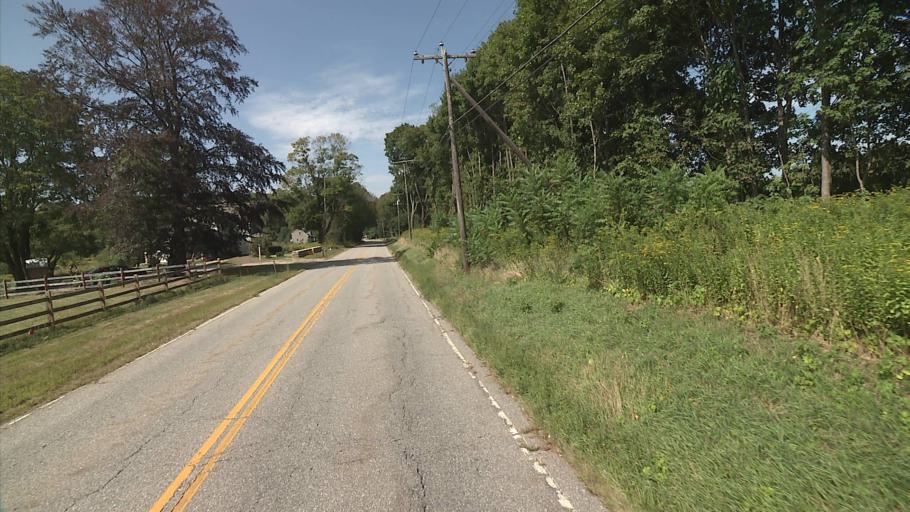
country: US
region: Connecticut
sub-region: Windham County
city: Willimantic
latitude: 41.6714
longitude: -72.2644
